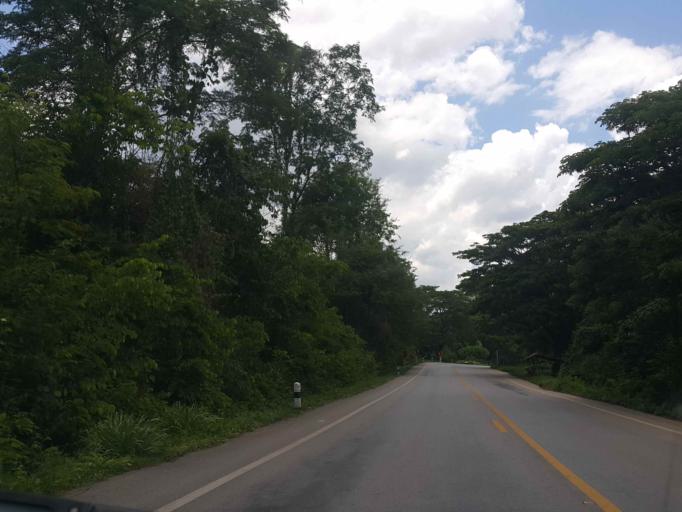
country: TH
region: Nan
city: Wiang Sa
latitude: 18.5172
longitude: 100.5926
